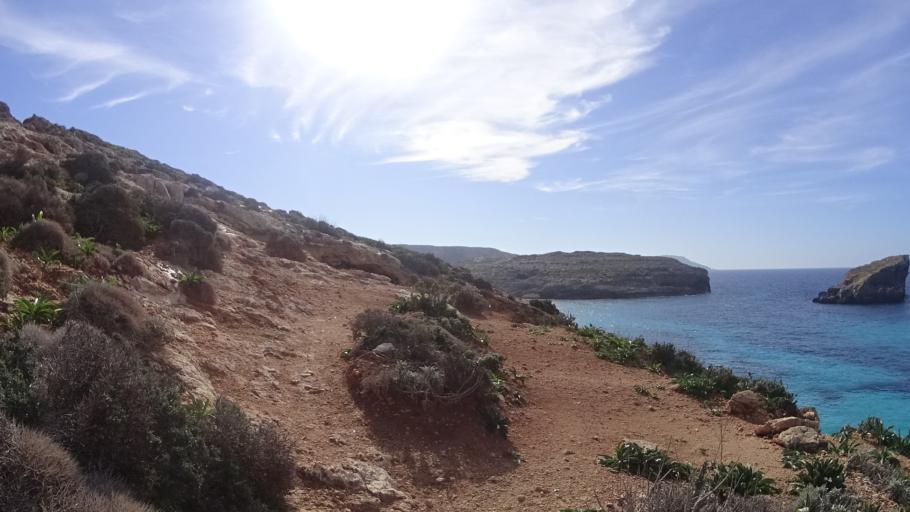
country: MT
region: Il-Qala
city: Qala
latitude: 36.0131
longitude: 14.3243
